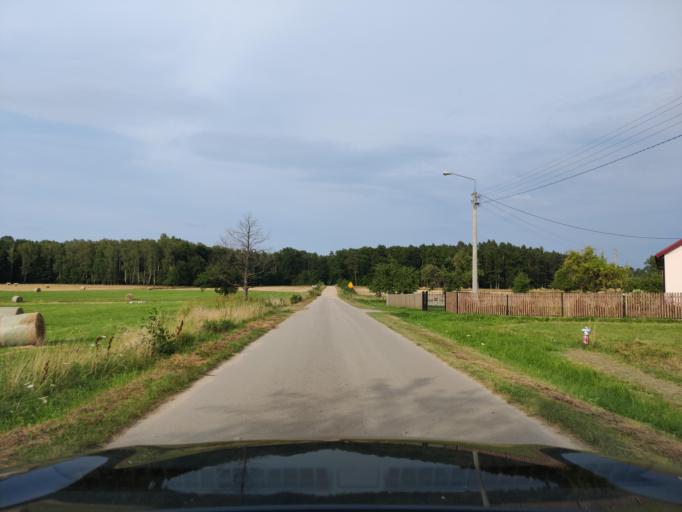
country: PL
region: Masovian Voivodeship
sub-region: Powiat pultuski
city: Obryte
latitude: 52.6978
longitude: 21.2058
